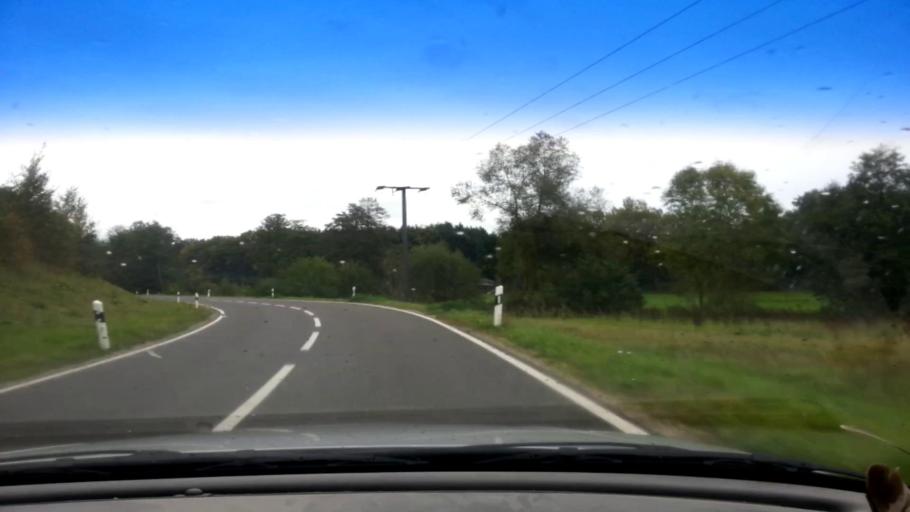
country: DE
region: Bavaria
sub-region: Regierungsbezirk Unterfranken
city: Stettfeld
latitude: 49.9924
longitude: 10.7532
